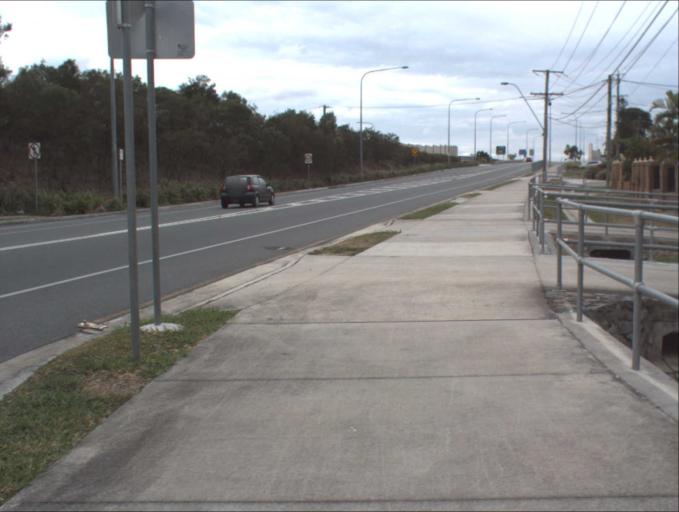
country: AU
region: Queensland
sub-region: Logan
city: Slacks Creek
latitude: -27.6418
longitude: 153.1414
